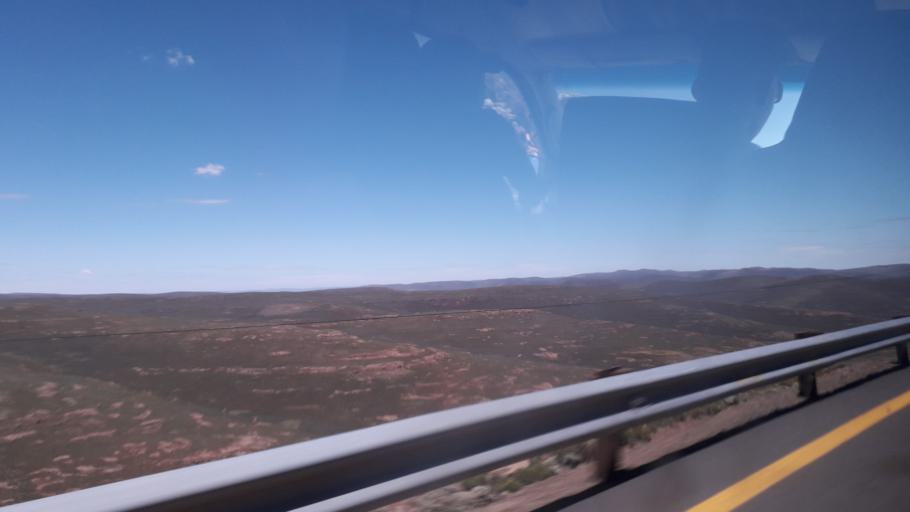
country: LS
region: Mokhotlong
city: Mokhotlong
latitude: -29.0199
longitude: 28.8524
